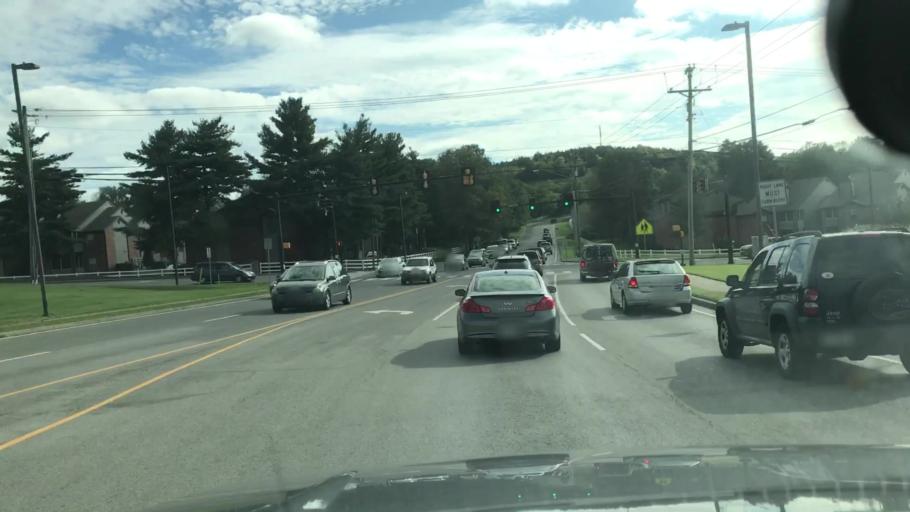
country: US
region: Tennessee
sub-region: Williamson County
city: Franklin
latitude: 35.9270
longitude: -86.8244
